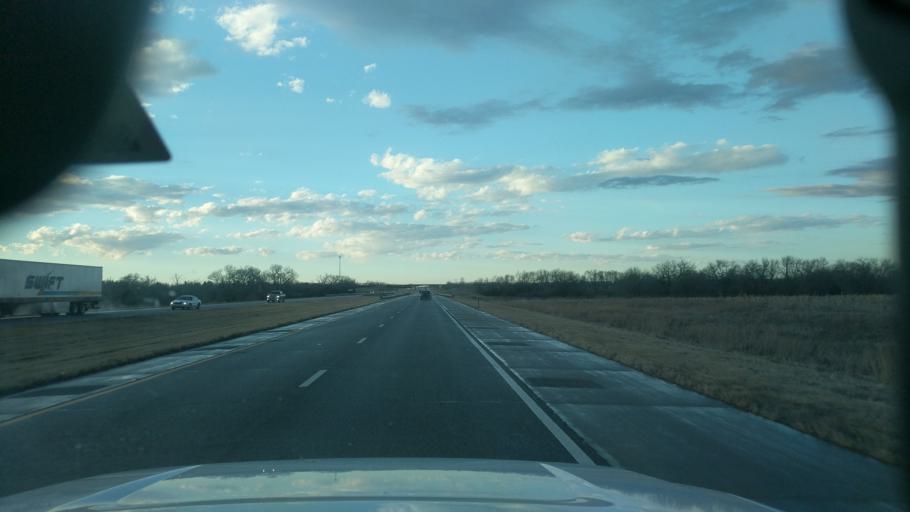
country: US
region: Kansas
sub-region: Harvey County
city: Hesston
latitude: 38.1829
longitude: -97.4603
